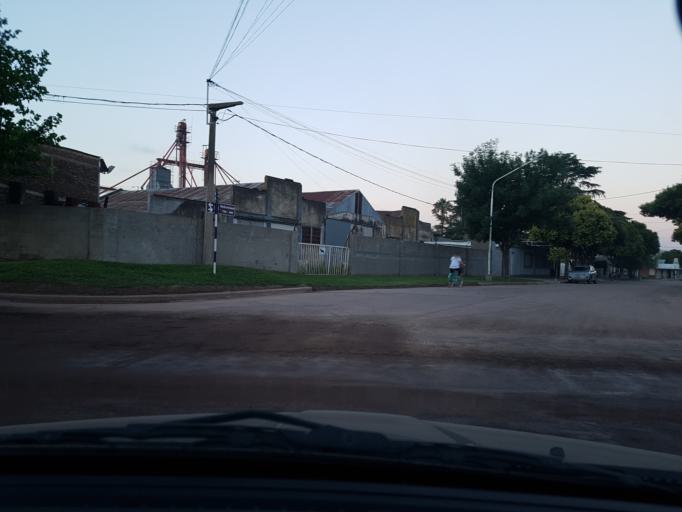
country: AR
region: Cordoba
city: General Cabrera
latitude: -32.7615
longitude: -63.7954
